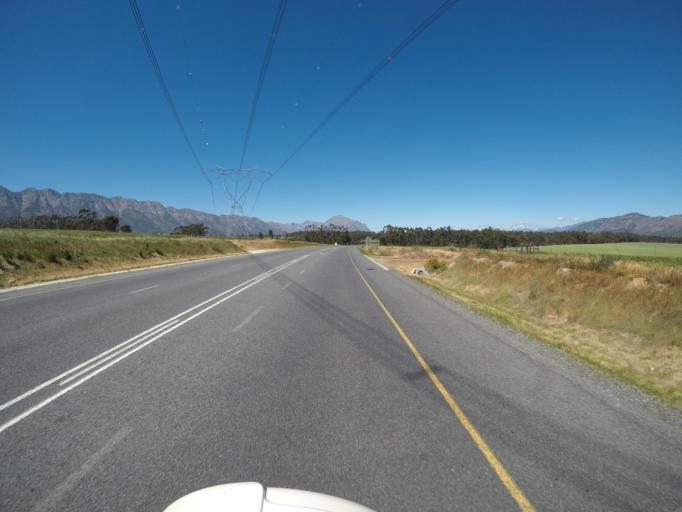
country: ZA
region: Western Cape
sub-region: Cape Winelands District Municipality
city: Ceres
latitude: -33.3290
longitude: 19.1556
